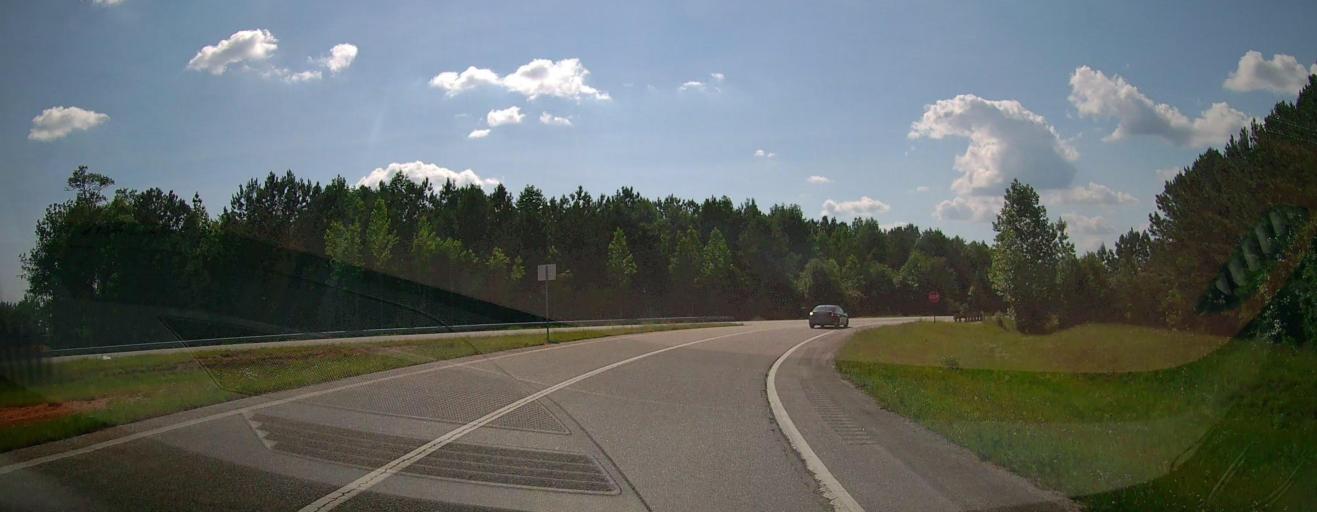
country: US
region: Georgia
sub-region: Henry County
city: Hampton
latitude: 33.3731
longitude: -84.3056
